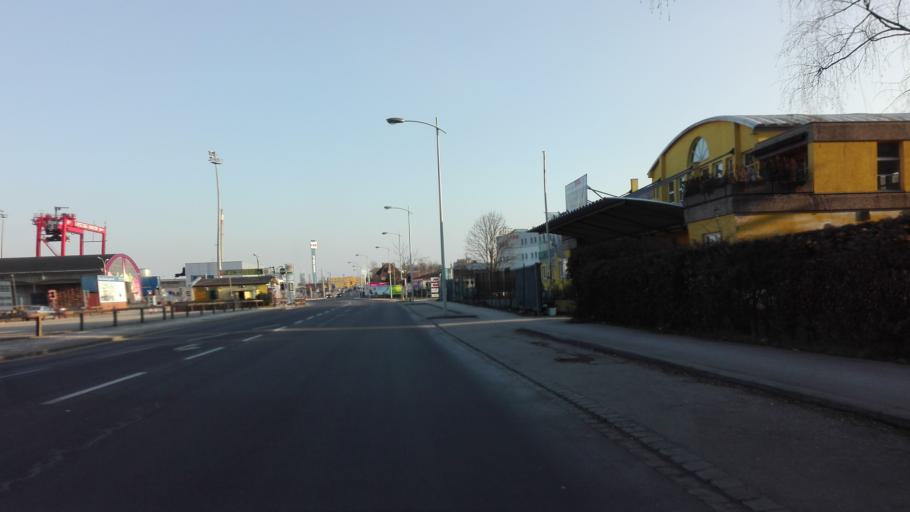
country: AT
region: Upper Austria
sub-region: Linz Stadt
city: Linz
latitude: 48.3125
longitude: 14.3130
